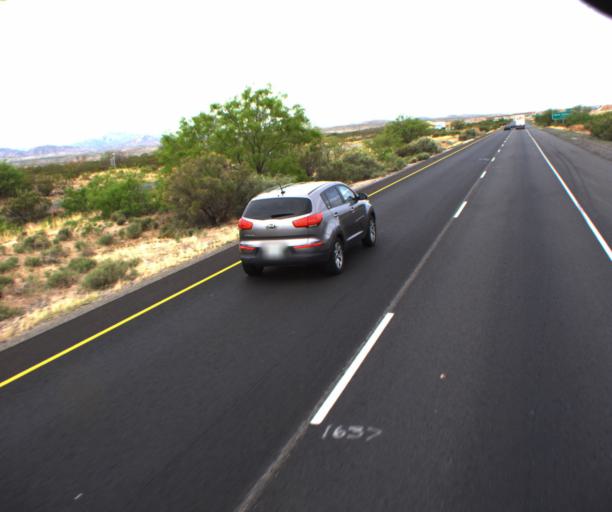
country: US
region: Arizona
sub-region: Cochise County
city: Mescal
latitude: 31.9800
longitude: -110.5242
